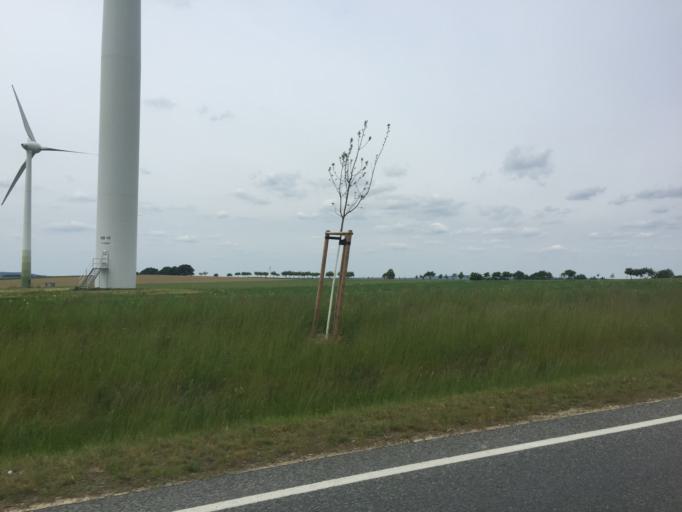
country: DE
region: Saxony
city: Reichenbach
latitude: 51.1449
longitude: 14.7747
